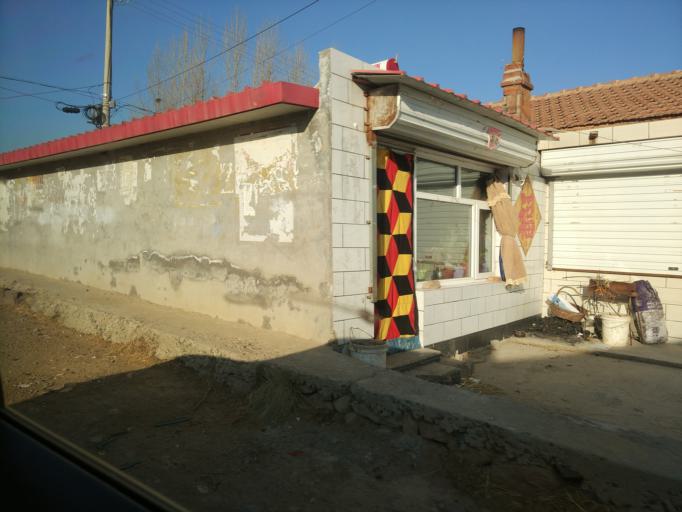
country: CN
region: Hebei
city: Xiwanzi
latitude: 40.8317
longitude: 115.5285
